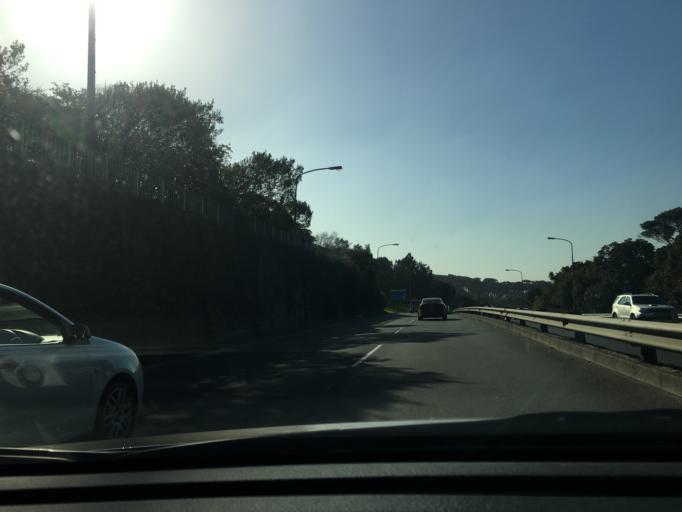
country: ZA
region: Western Cape
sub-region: City of Cape Town
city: Rosebank
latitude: -33.9569
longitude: 18.4638
